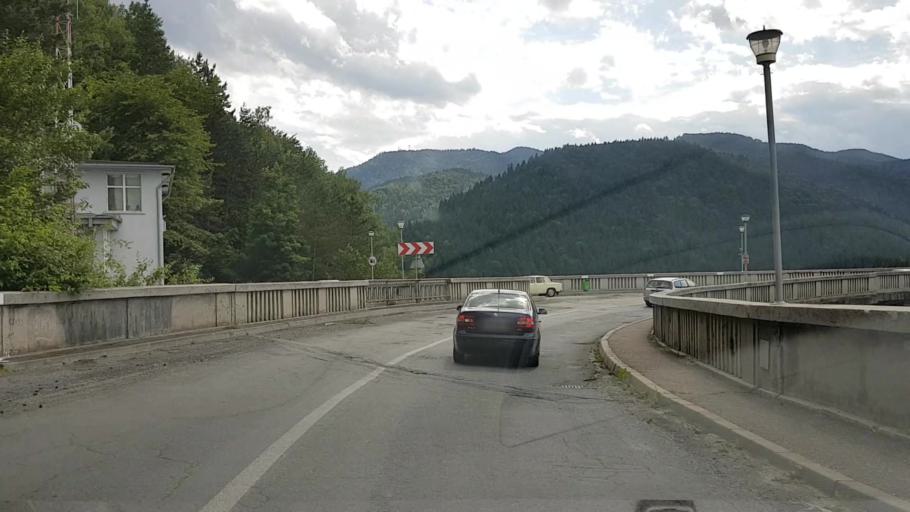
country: RO
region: Neamt
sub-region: Comuna Bicaz
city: Dodeni
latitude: 46.9377
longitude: 26.1055
